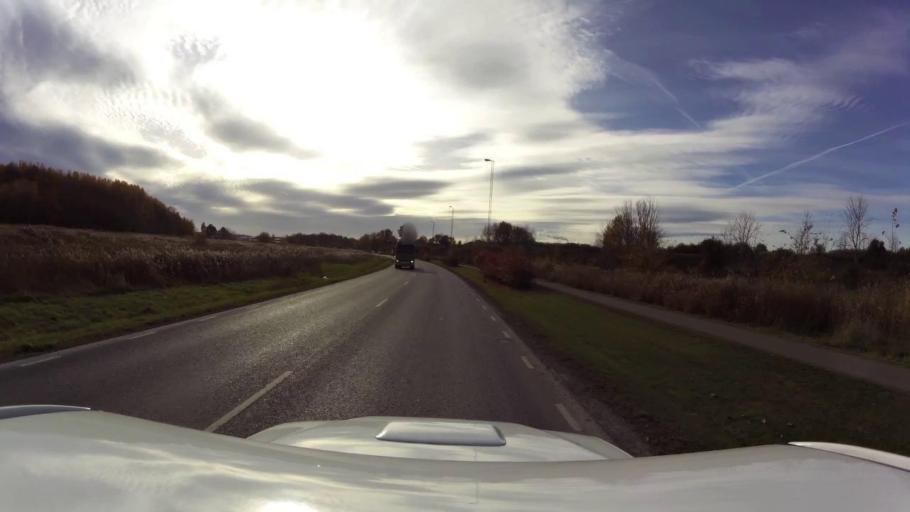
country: SE
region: OEstergoetland
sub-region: Linkopings Kommun
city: Linkoping
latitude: 58.4285
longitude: 15.6391
